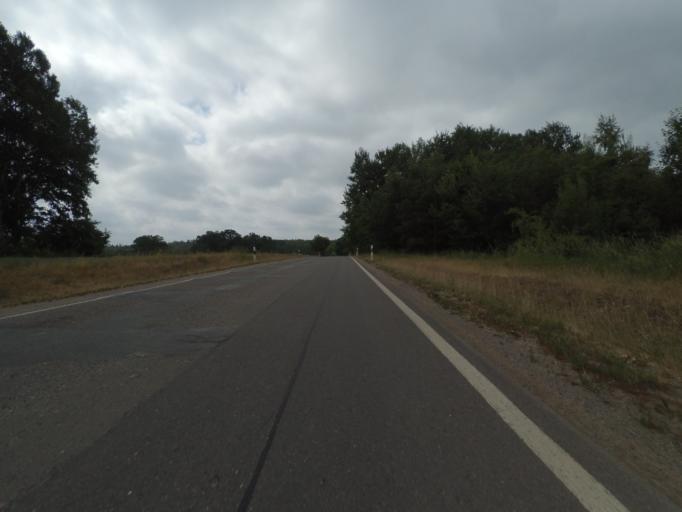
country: DE
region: Mecklenburg-Vorpommern
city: Krakow am See
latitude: 53.6297
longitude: 12.3464
